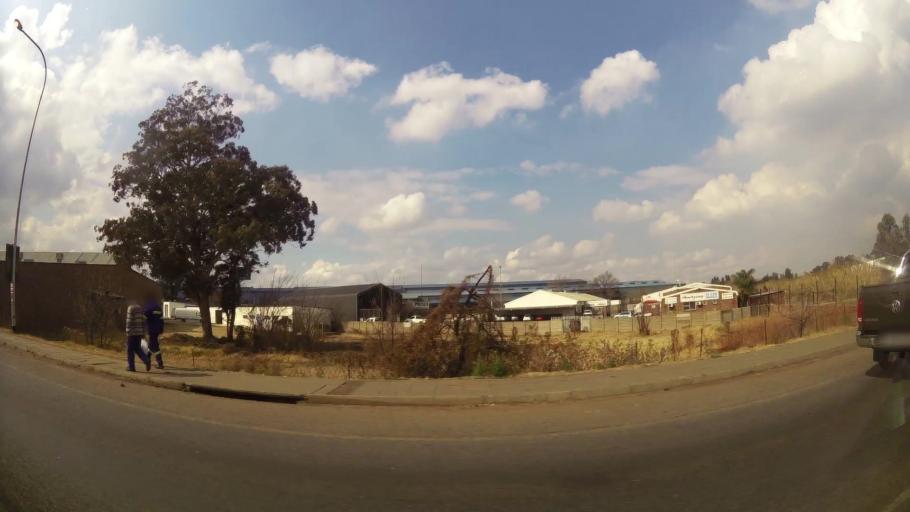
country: ZA
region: Gauteng
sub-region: Sedibeng District Municipality
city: Vereeniging
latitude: -26.6639
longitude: 27.9341
